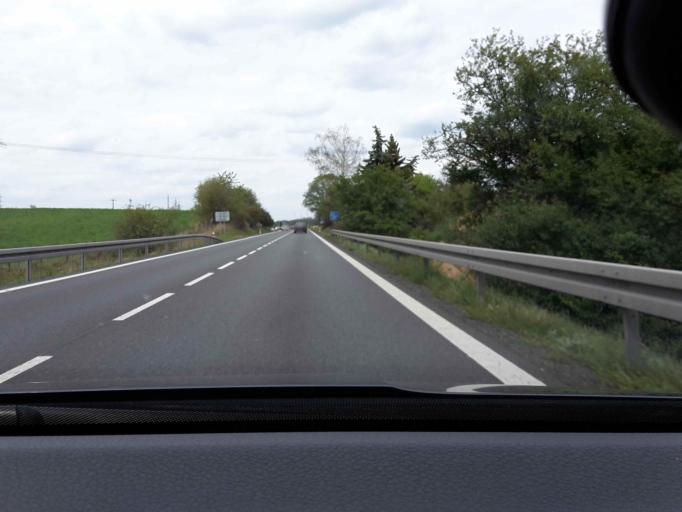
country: CZ
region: Central Bohemia
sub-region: Okres Benesov
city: Benesov
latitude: 49.7908
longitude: 14.6786
